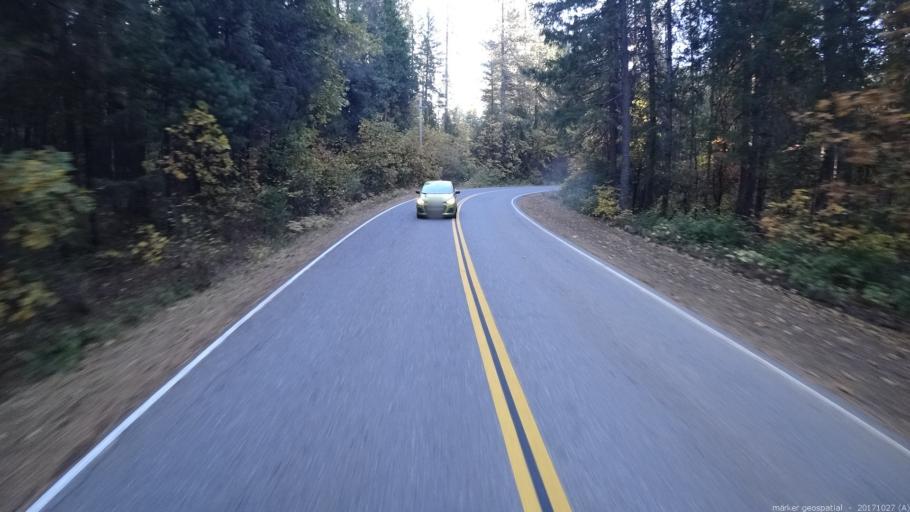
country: US
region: California
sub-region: Shasta County
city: Burney
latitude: 40.9919
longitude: -121.9200
